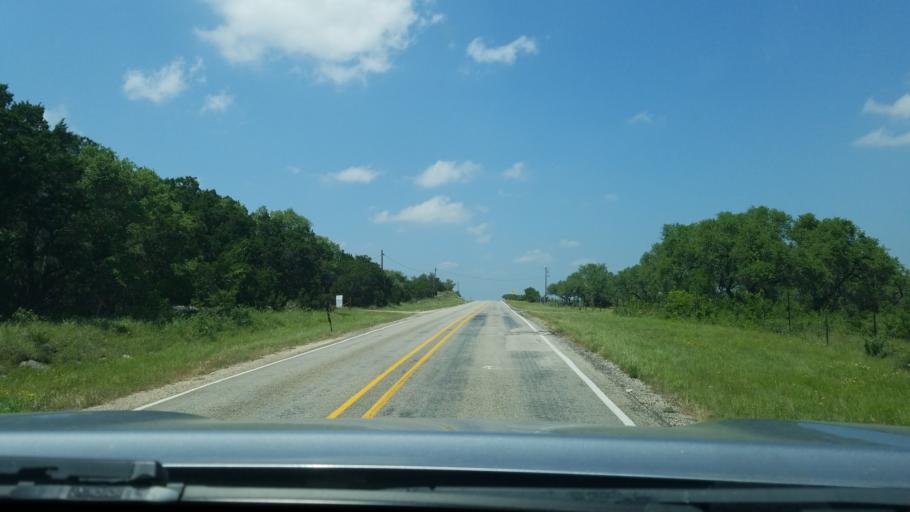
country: US
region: Texas
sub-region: Hays County
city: Woodcreek
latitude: 30.0729
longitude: -98.2207
